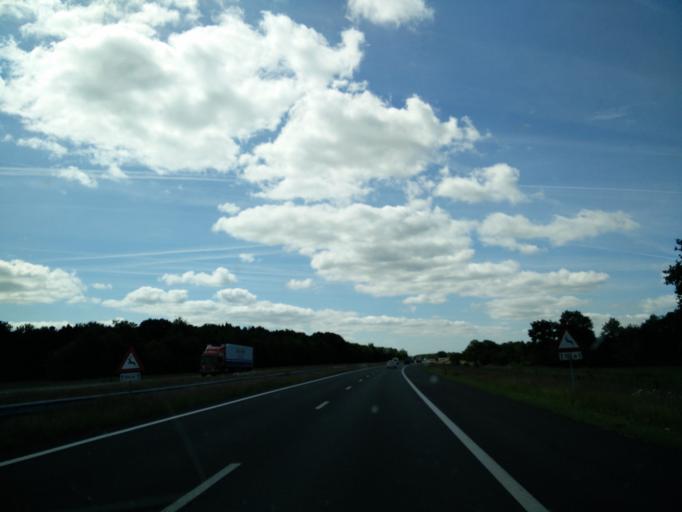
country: NL
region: Drenthe
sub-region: Gemeente Assen
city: Assen
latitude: 52.9020
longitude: 6.5314
